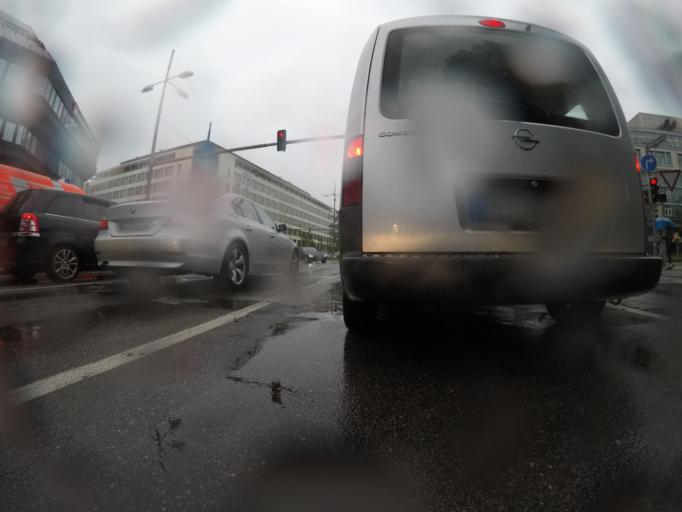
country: DE
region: Baden-Wuerttemberg
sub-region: Regierungsbezirk Stuttgart
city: Stuttgart
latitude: 48.7753
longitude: 9.1716
